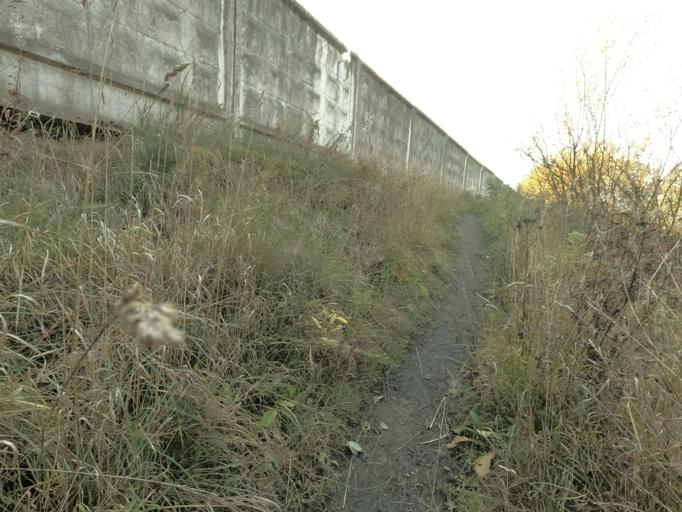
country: RU
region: Leningrad
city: Mga
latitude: 59.7447
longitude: 31.0647
